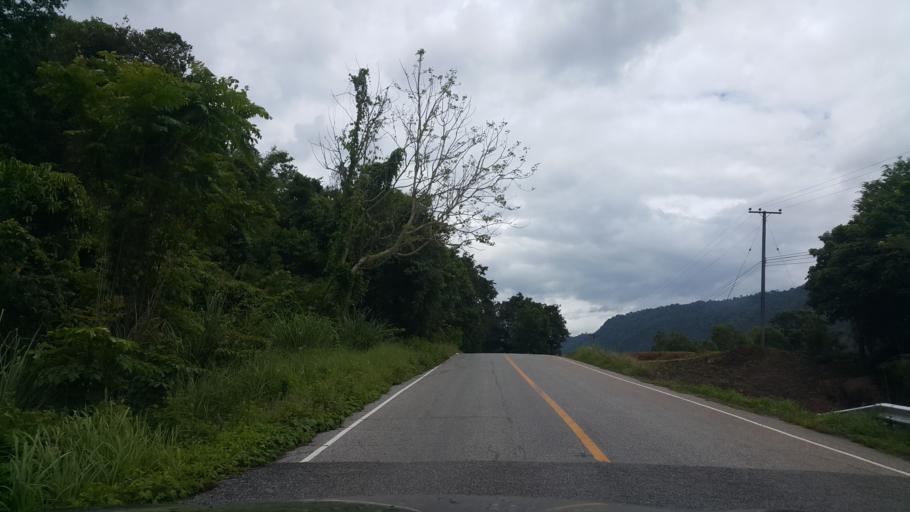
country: TH
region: Phitsanulok
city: Chat Trakan
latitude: 17.3439
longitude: 100.7158
